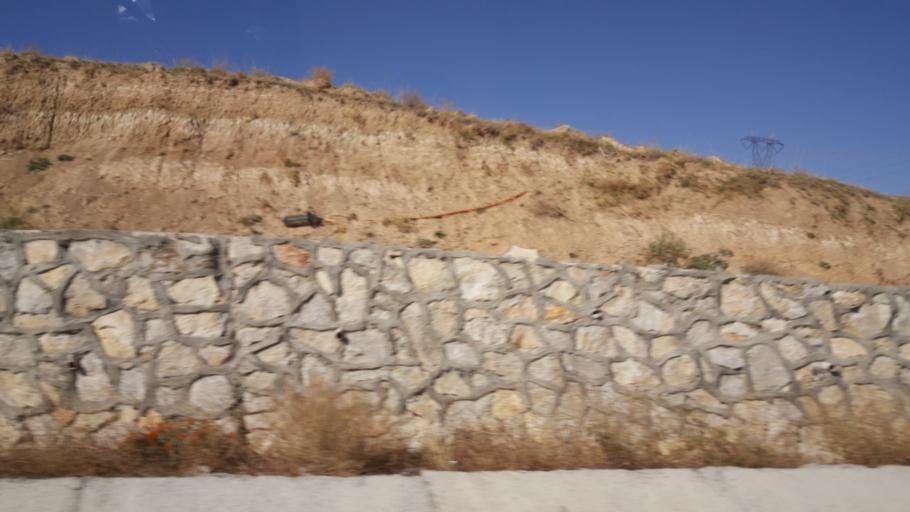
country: TR
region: Ankara
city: Ikizce
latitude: 39.5928
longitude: 32.6696
